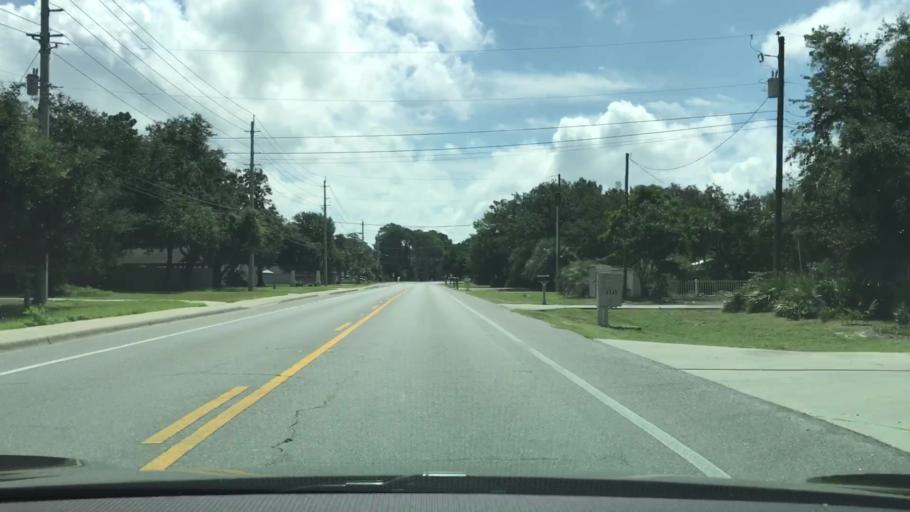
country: US
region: Florida
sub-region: Bay County
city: Lower Grand Lagoon
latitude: 30.1574
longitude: -85.7585
